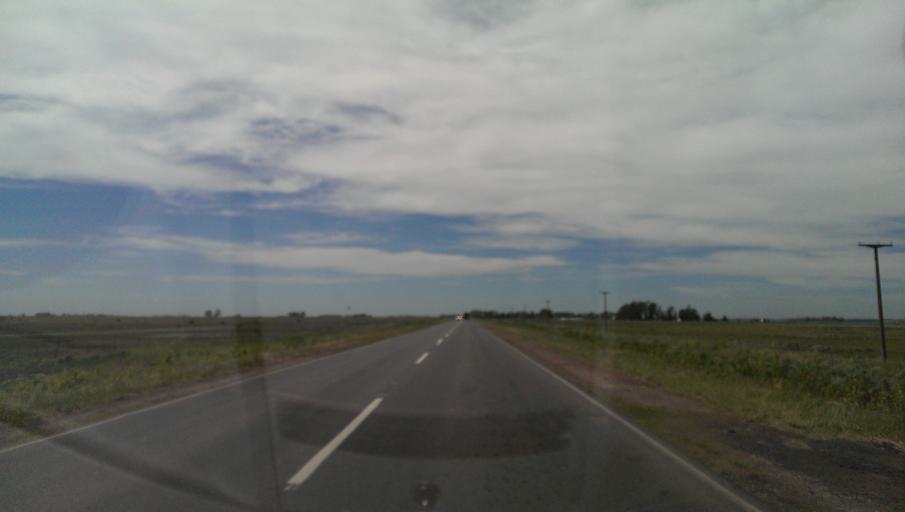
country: AR
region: Buenos Aires
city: Olavarria
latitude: -37.0340
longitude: -60.4279
